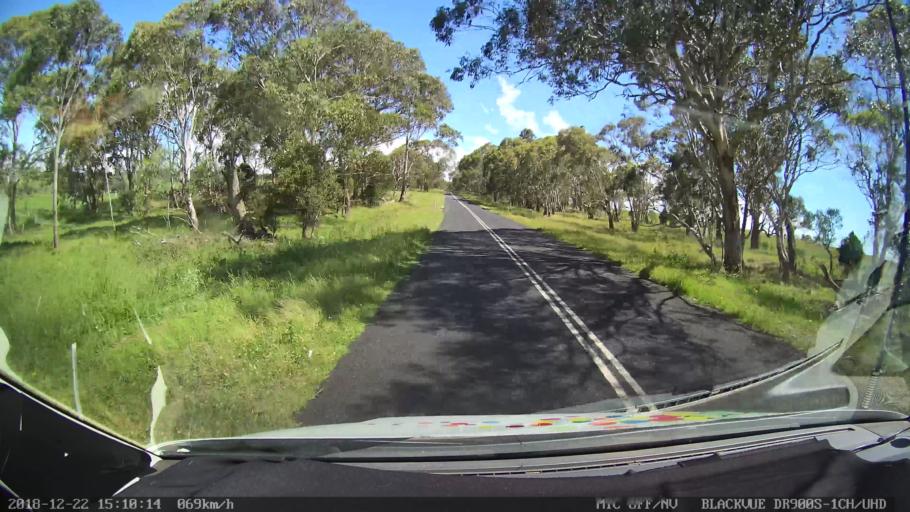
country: AU
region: New South Wales
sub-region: Bellingen
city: Dorrigo
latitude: -30.3326
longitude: 152.4052
